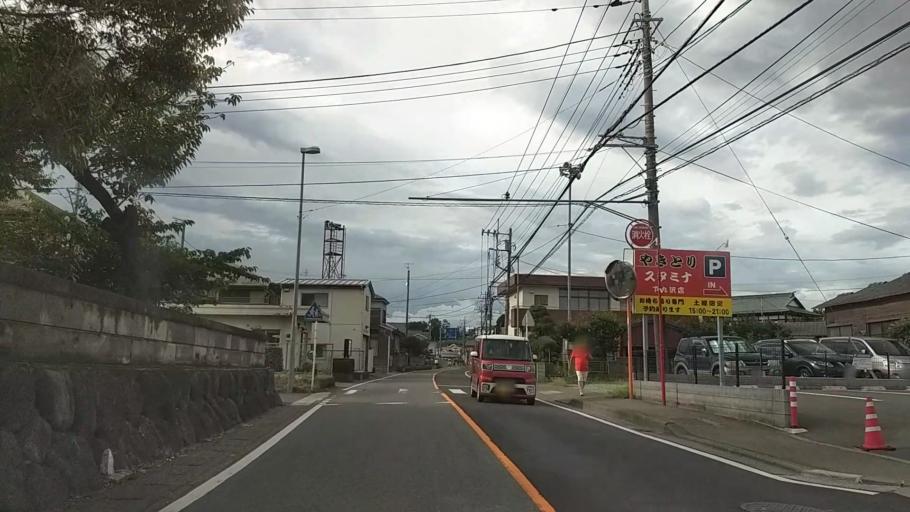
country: JP
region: Tokyo
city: Hachioji
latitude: 35.5724
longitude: 139.3405
